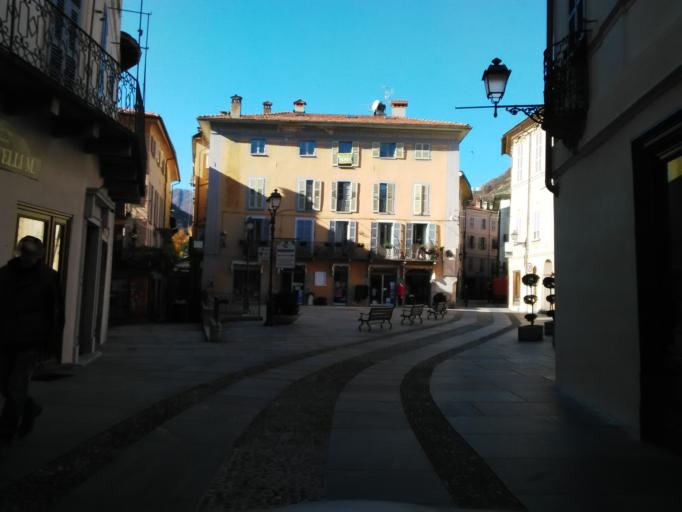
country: IT
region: Piedmont
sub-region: Provincia di Vercelli
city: Varallo
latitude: 45.8158
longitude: 8.2521
